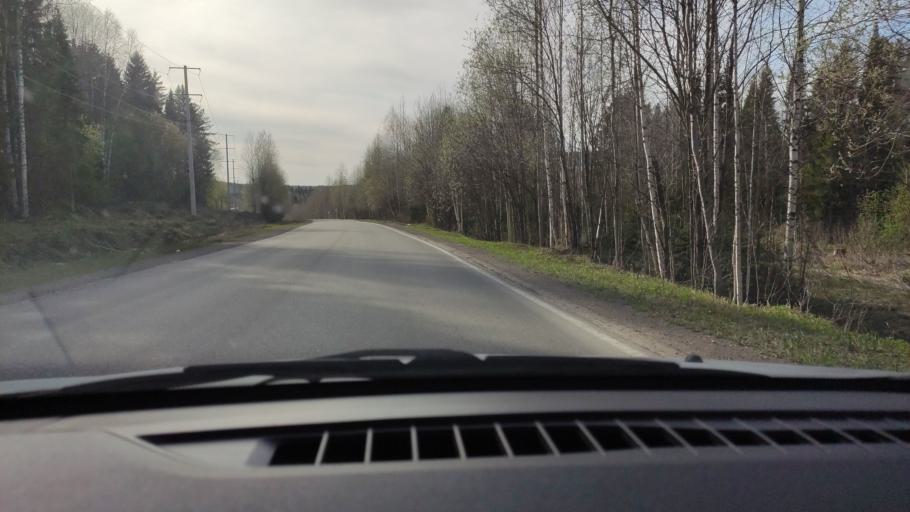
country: RU
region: Perm
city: Novyye Lyady
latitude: 57.9570
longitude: 56.5629
